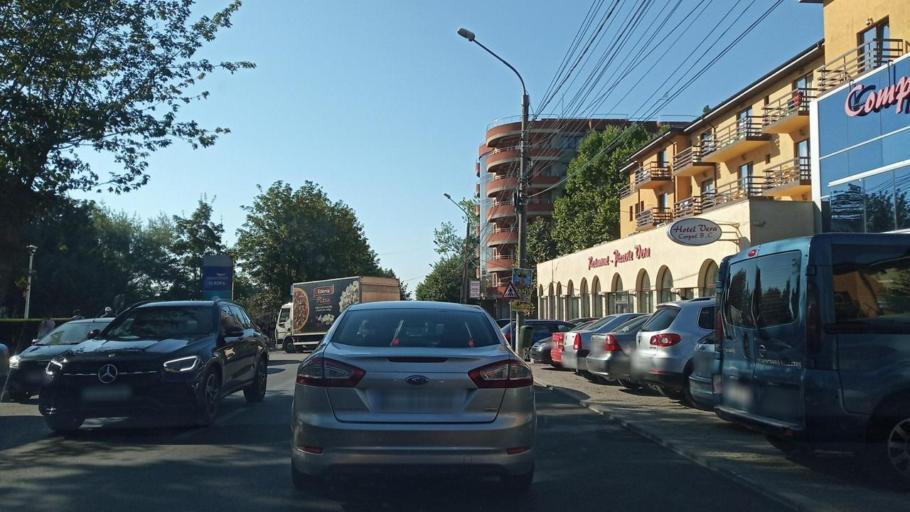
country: RO
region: Constanta
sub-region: Oras Eforie
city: Eforie Nord
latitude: 44.0624
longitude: 28.6350
